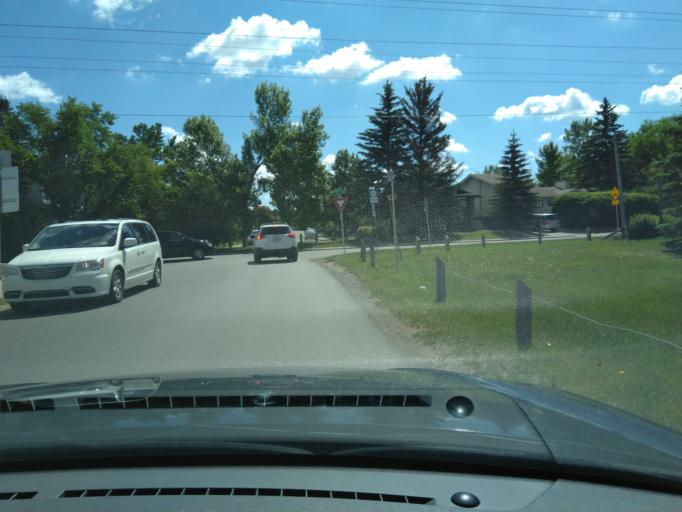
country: CA
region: Alberta
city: Calgary
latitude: 51.0702
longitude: -114.1649
